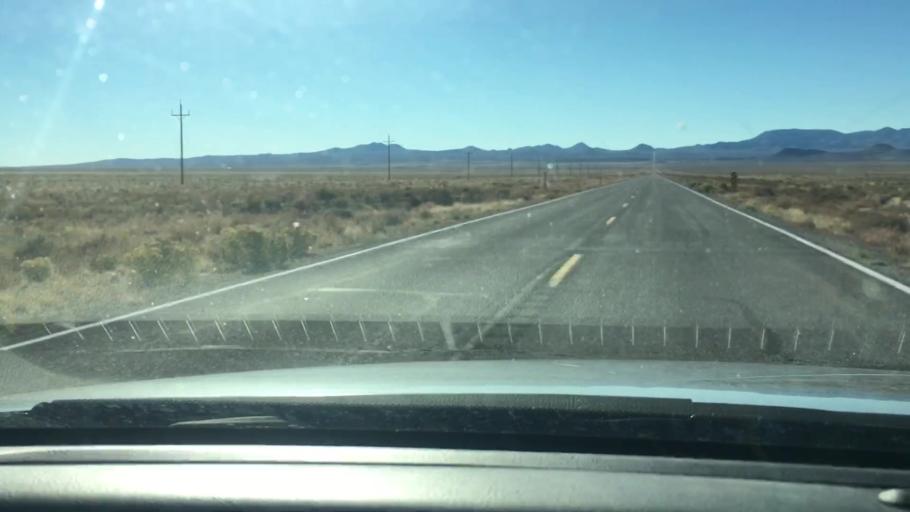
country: US
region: Nevada
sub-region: Nye County
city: Tonopah
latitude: 38.1564
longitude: -116.5274
